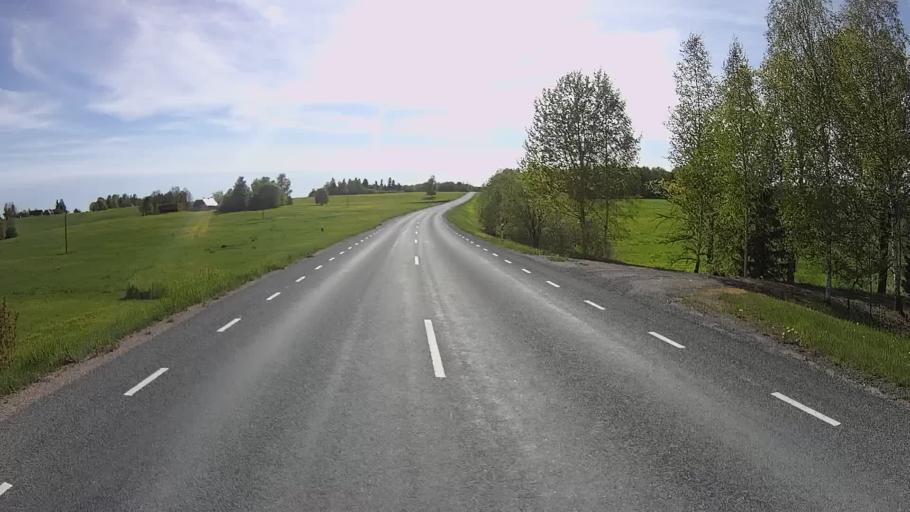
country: EE
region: Vorumaa
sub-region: Antsla vald
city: Vana-Antsla
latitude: 57.9533
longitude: 26.4427
